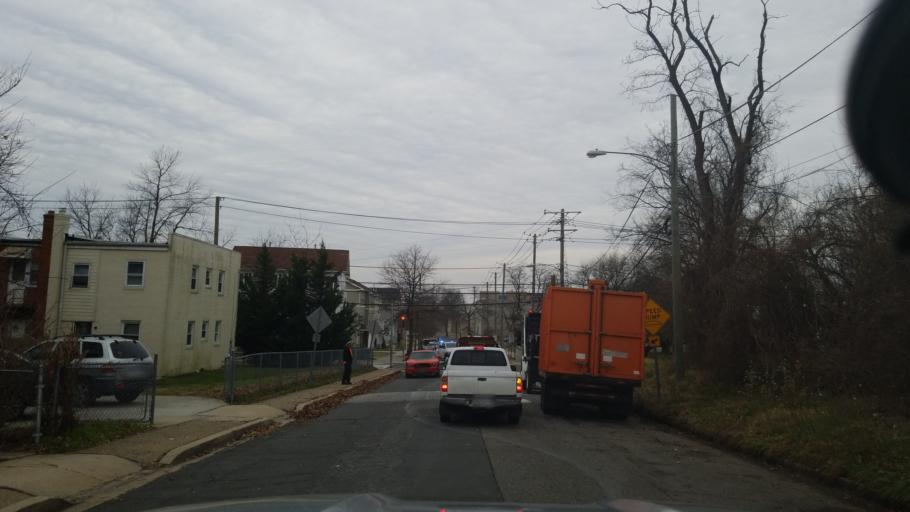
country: US
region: Maryland
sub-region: Prince George's County
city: Hillcrest Heights
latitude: 38.8507
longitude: -76.9803
